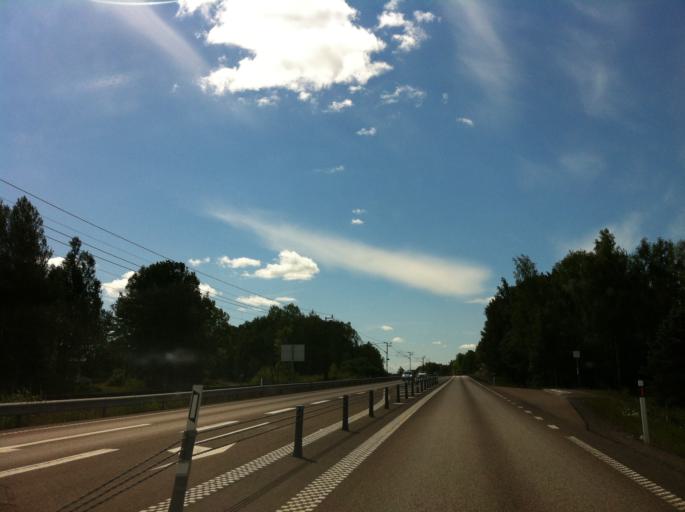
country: SE
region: Vaestra Goetaland
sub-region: Melleruds Kommun
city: Mellerud
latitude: 58.8642
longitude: 12.5610
